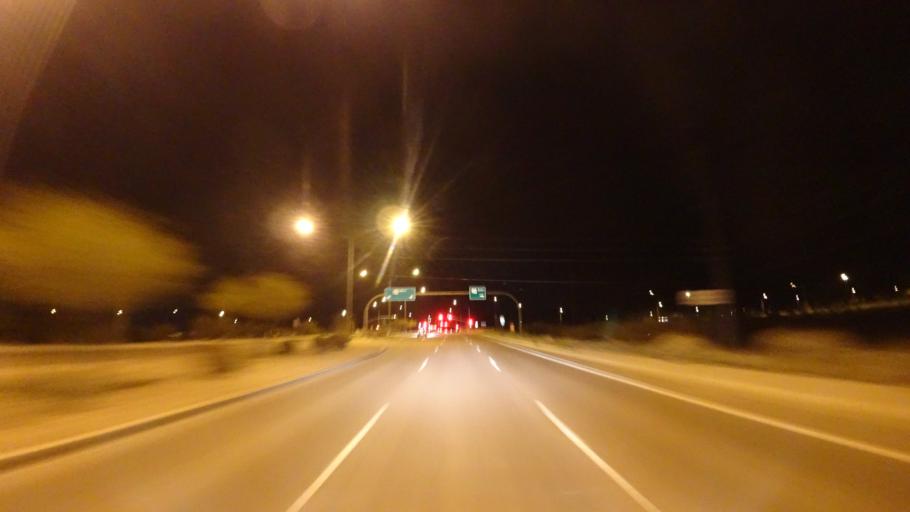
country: US
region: Arizona
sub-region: Maricopa County
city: Mesa
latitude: 33.4794
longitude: -111.7183
